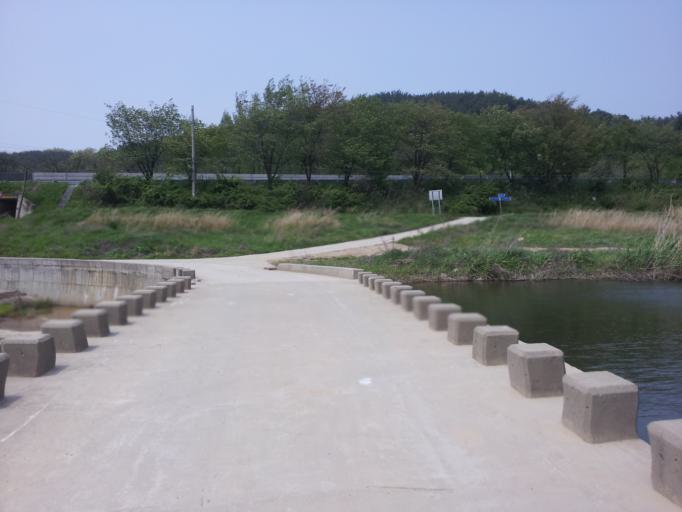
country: KR
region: Daejeon
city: Daejeon
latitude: 36.2599
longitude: 127.2842
